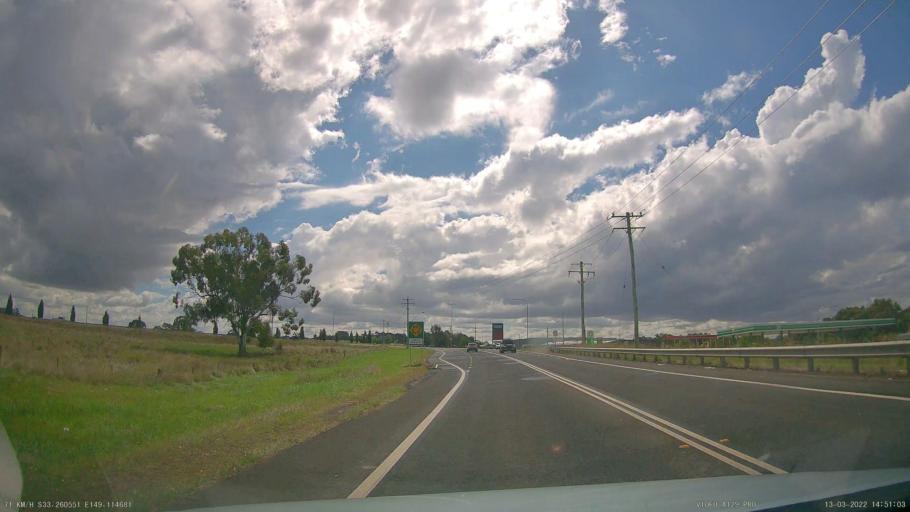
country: AU
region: New South Wales
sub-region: Orange Municipality
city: Orange
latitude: -33.2606
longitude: 149.1144
